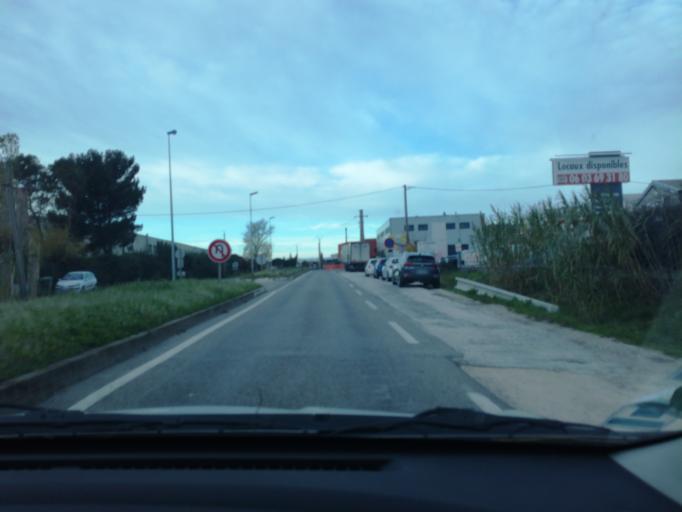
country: FR
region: Provence-Alpes-Cote d'Azur
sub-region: Departement du Var
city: La Farlede
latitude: 43.1550
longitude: 6.0470
